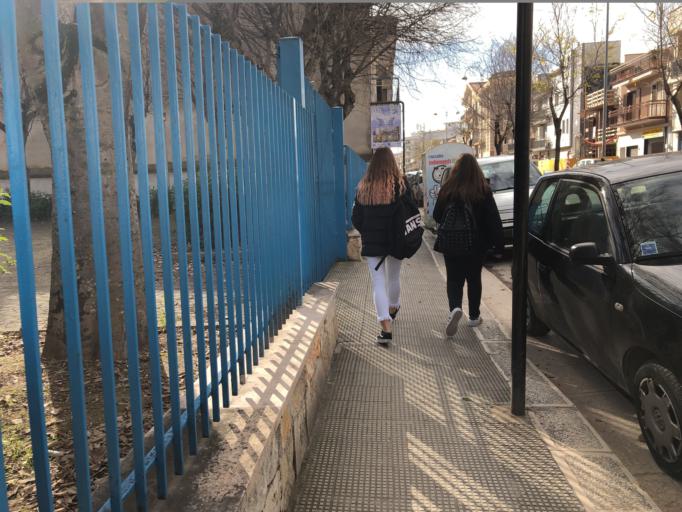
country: IT
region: Apulia
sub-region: Provincia di Barletta - Andria - Trani
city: Andria
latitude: 41.2246
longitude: 16.3070
